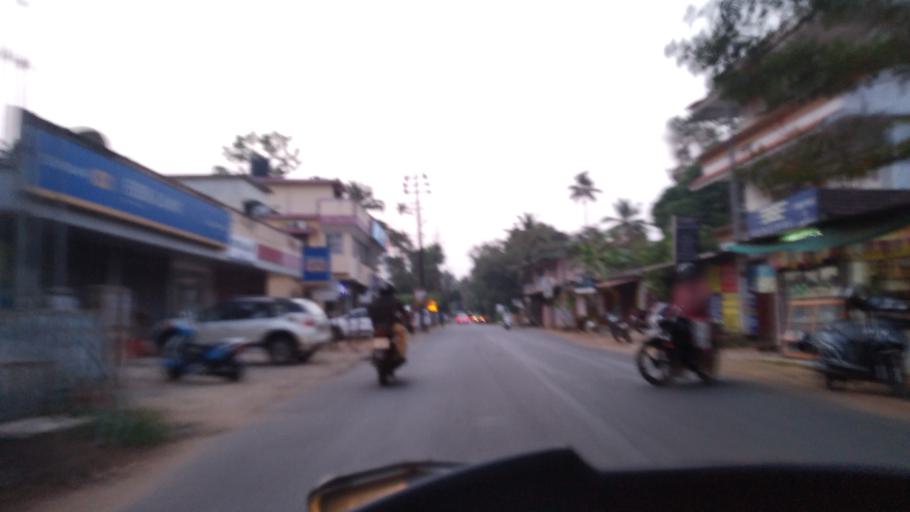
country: IN
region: Kerala
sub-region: Kottayam
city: Kottayam
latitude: 9.5934
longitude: 76.4333
